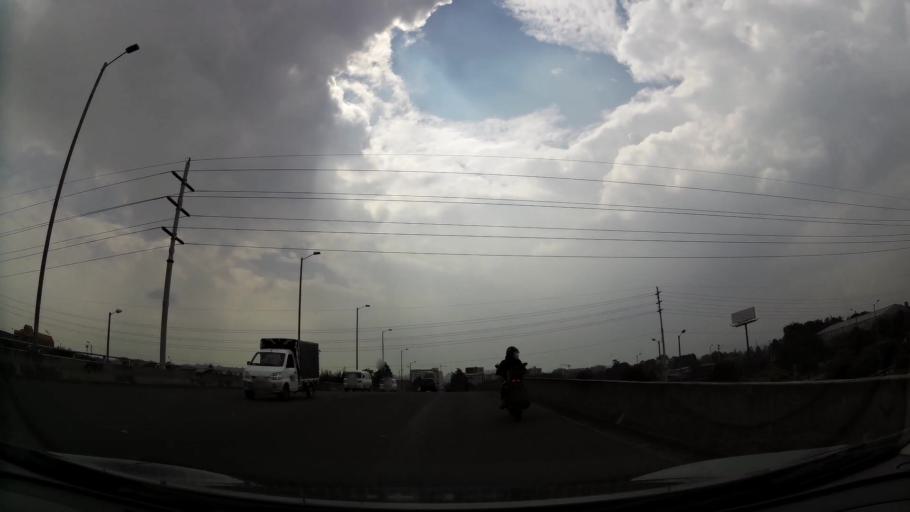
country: CO
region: Bogota D.C.
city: Barrio San Luis
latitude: 4.7379
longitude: -74.0479
